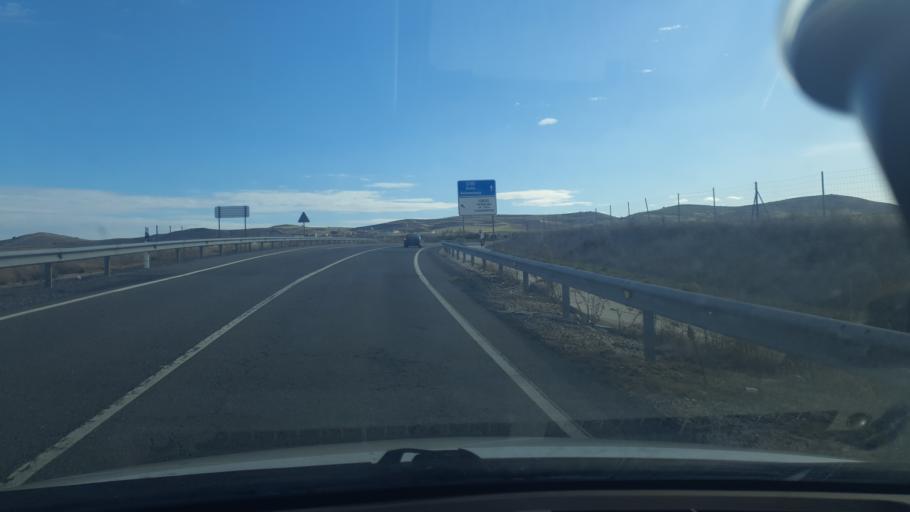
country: ES
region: Castille and Leon
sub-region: Provincia de Avila
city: Penalba de Avila
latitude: 40.7845
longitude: -4.7569
